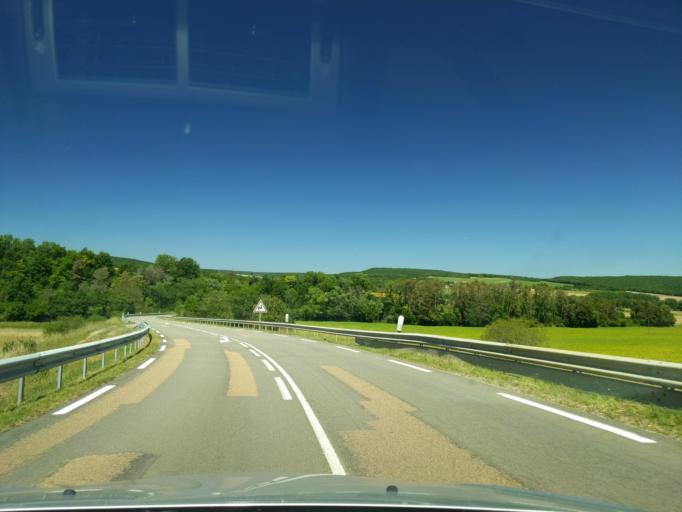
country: FR
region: Bourgogne
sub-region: Departement de la Cote-d'Or
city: Is-sur-Tille
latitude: 47.5079
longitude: 5.0764
